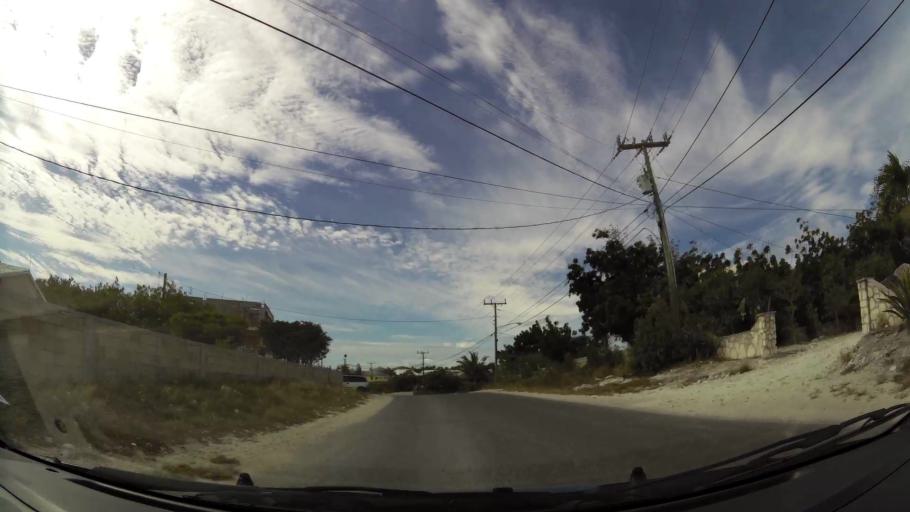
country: BS
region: Mayaguana
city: Abraham's Bay
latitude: 21.7779
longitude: -72.2429
